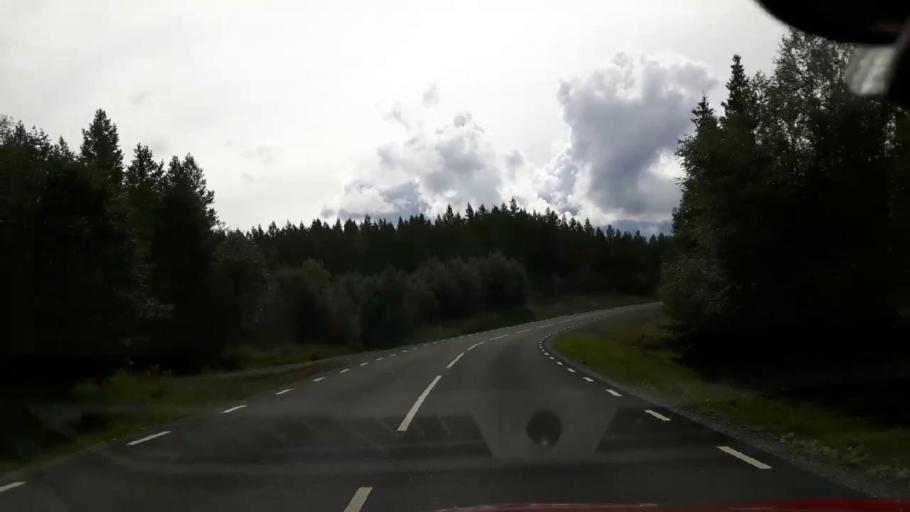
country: NO
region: Nord-Trondelag
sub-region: Lierne
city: Sandvika
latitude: 64.6335
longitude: 14.1412
